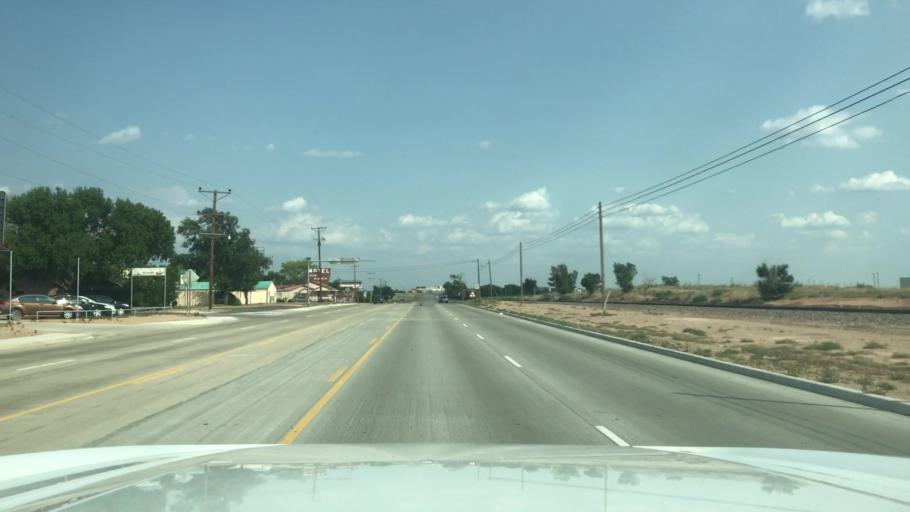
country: US
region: Texas
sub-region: Dallam County
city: Dalhart
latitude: 36.0504
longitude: -102.4999
